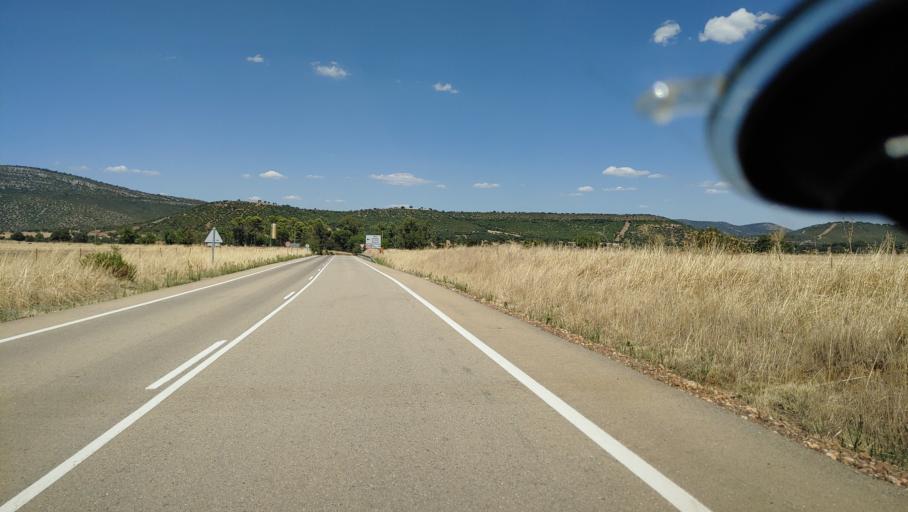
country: ES
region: Castille-La Mancha
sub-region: Provincia de Ciudad Real
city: Saceruela
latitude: 39.0139
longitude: -4.4953
